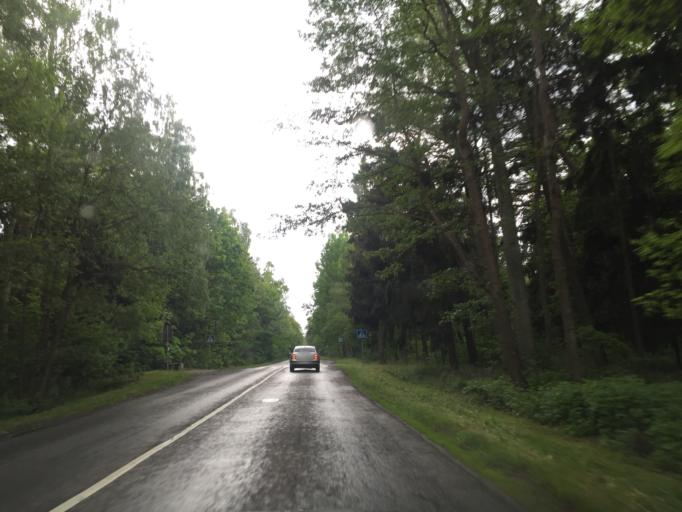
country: LT
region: Klaipedos apskritis
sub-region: Klaipeda
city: Klaipeda
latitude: 55.7428
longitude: 21.0948
